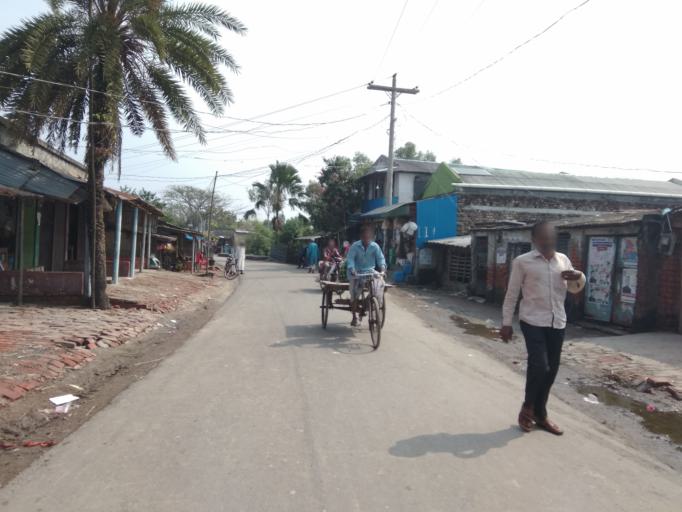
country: IN
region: West Bengal
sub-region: North 24 Parganas
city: Gosaba
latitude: 22.2296
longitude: 89.1567
